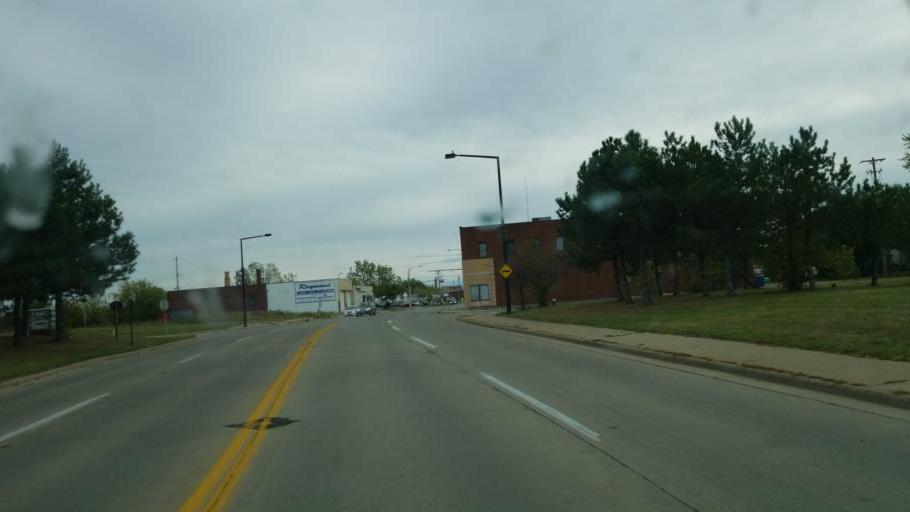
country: US
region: Ohio
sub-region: Lorain County
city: Lorain
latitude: 41.4600
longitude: -82.1704
